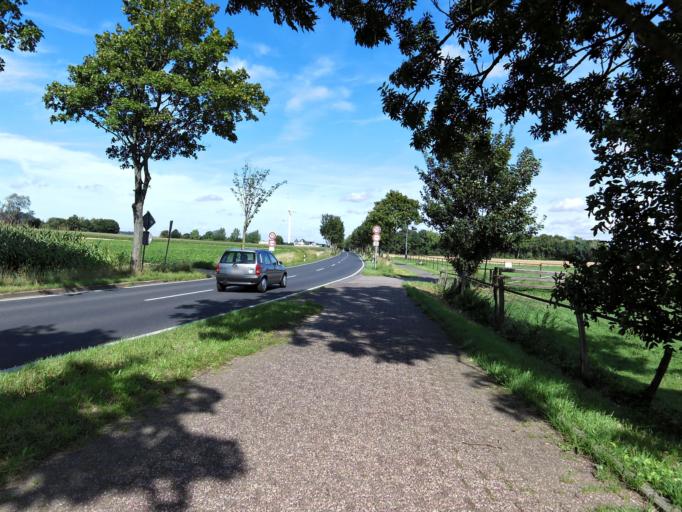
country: DE
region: North Rhine-Westphalia
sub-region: Regierungsbezirk Koln
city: Alsdorf
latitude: 50.8840
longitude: 6.1519
